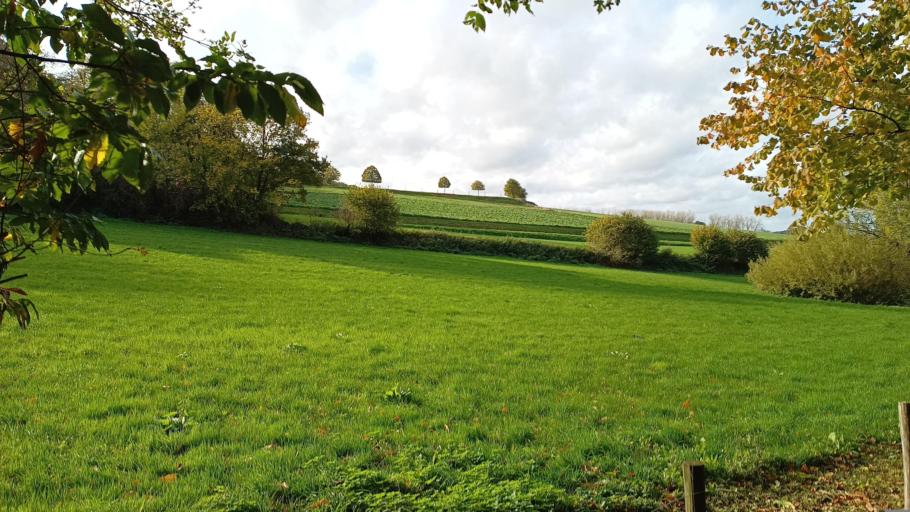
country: FR
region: Nord-Pas-de-Calais
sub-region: Departement du Nord
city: Nieppe
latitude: 50.7829
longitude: 2.8165
